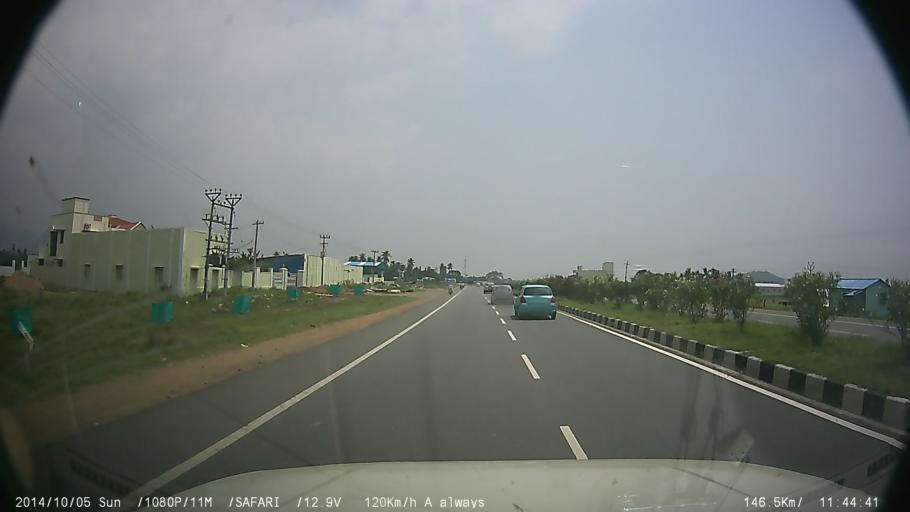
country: IN
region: Tamil Nadu
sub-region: Salem
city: Attur
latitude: 11.5922
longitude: 78.6401
